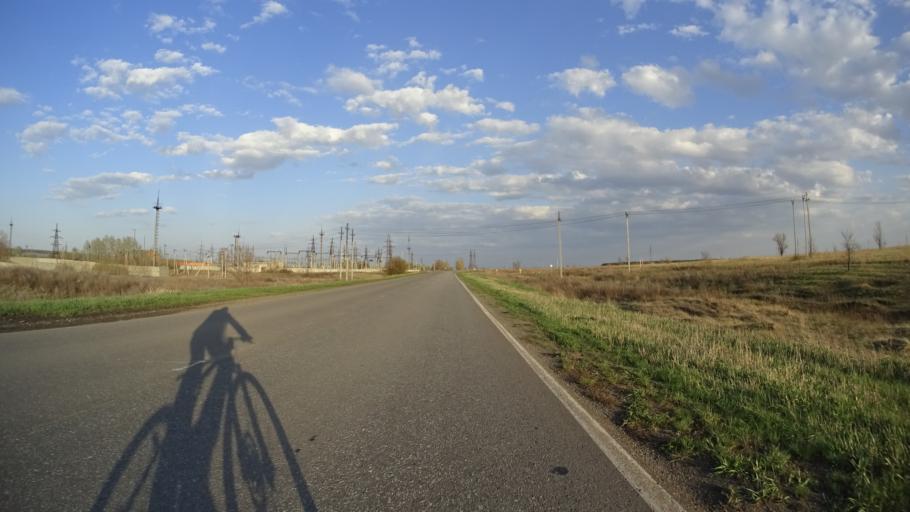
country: RU
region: Chelyabinsk
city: Troitsk
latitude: 54.0596
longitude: 61.5796
